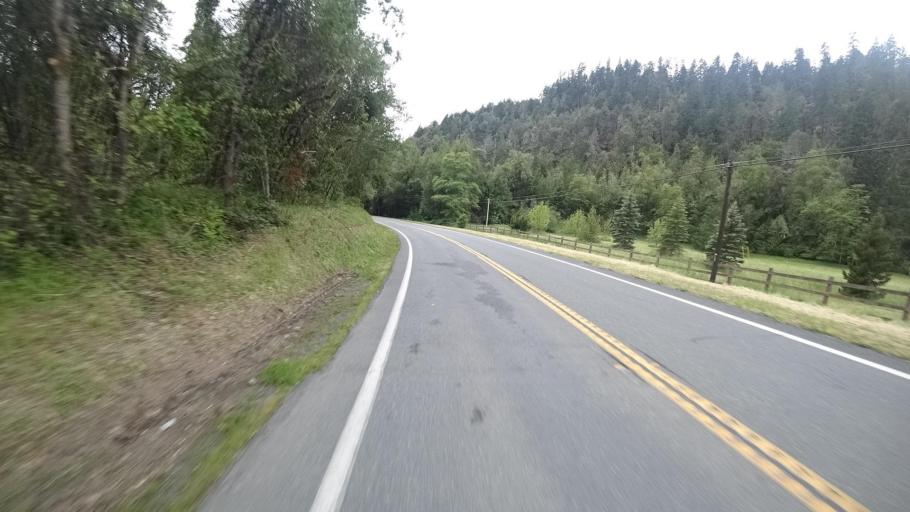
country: US
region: California
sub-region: Humboldt County
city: Willow Creek
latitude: 40.9552
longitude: -123.6433
